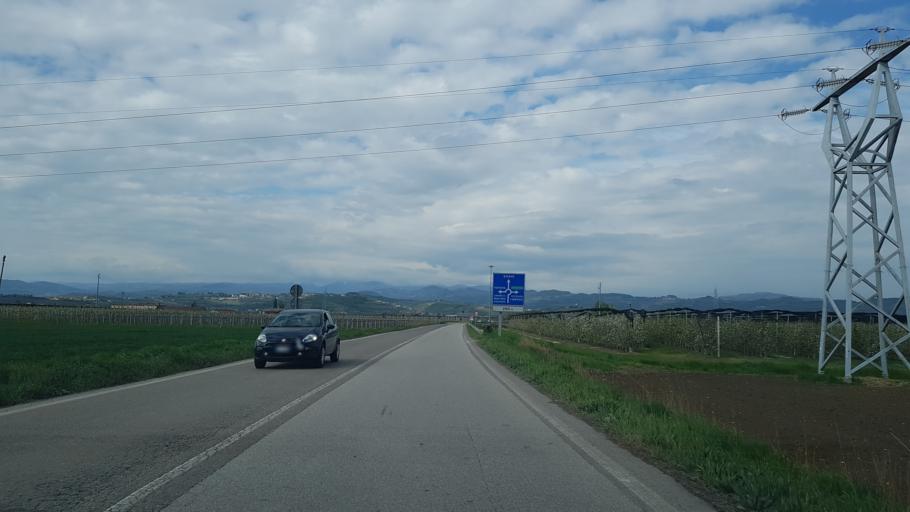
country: IT
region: Veneto
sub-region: Provincia di Verona
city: Belfiore
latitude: 45.3884
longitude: 11.2125
